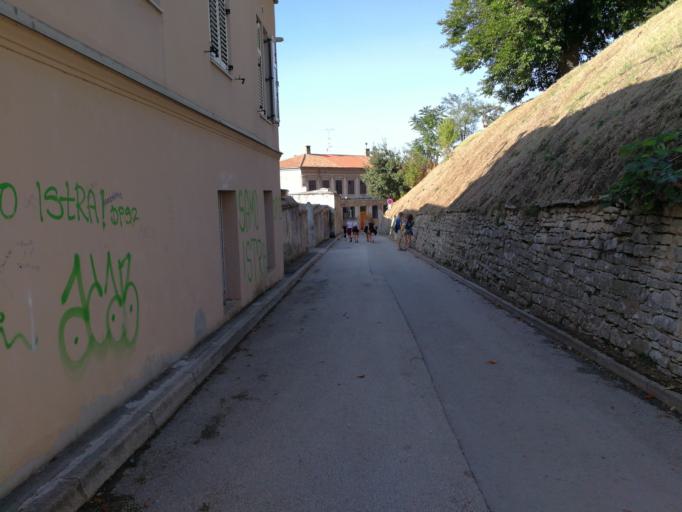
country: HR
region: Istarska
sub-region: Grad Pula
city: Pula
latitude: 44.8703
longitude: 13.8445
